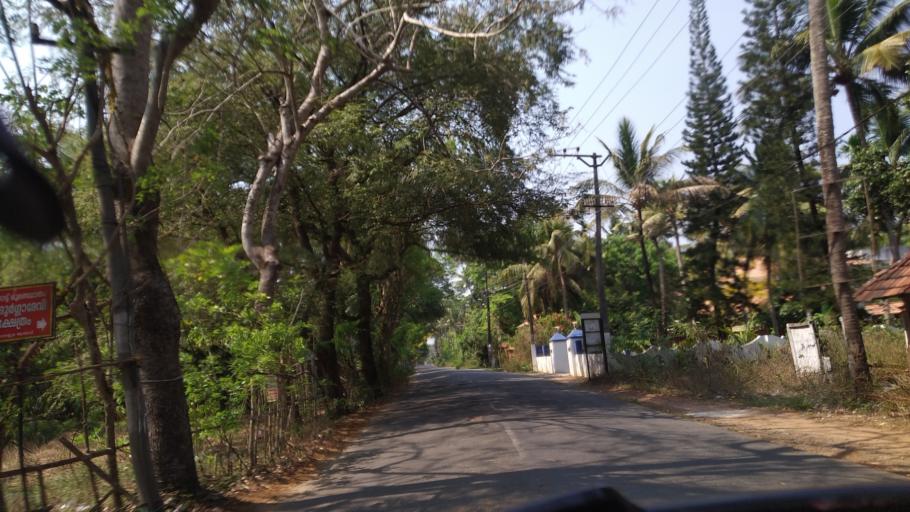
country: IN
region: Kerala
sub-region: Thrissur District
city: Kodungallur
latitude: 10.2557
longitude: 76.1464
